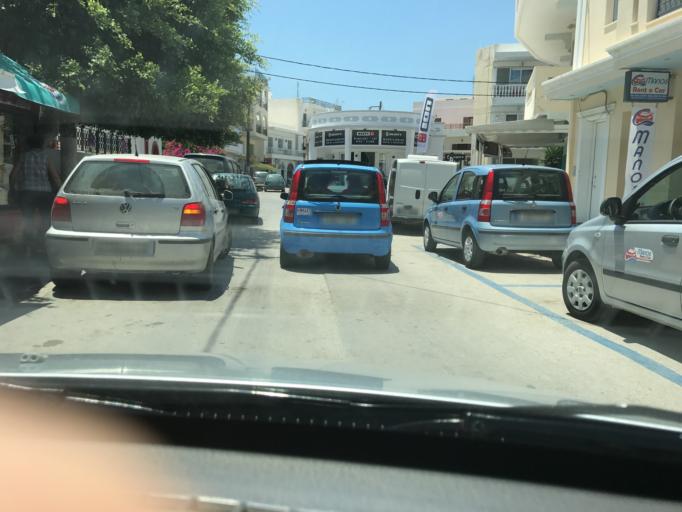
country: GR
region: South Aegean
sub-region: Nomos Dodekanisou
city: Karpathos
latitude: 35.5068
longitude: 27.2133
